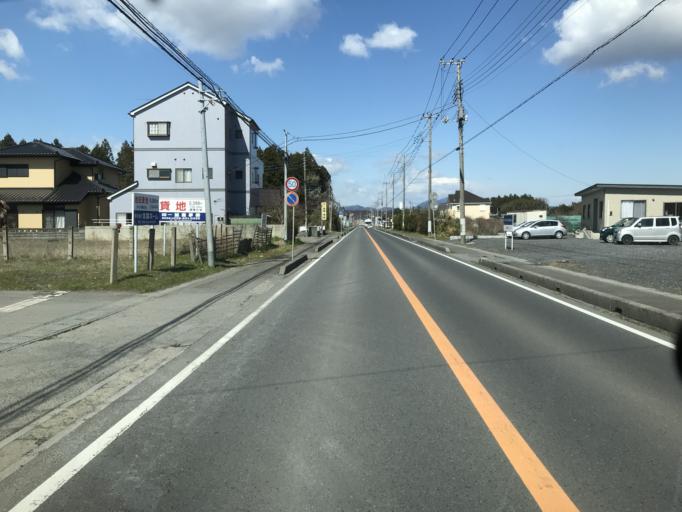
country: JP
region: Ibaraki
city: Ishioka
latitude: 36.1049
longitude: 140.2622
